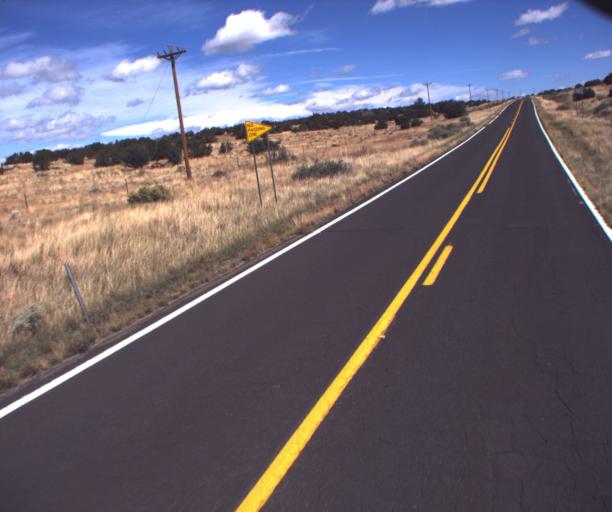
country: US
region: New Mexico
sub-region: McKinley County
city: Zuni Pueblo
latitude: 34.9833
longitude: -109.1243
